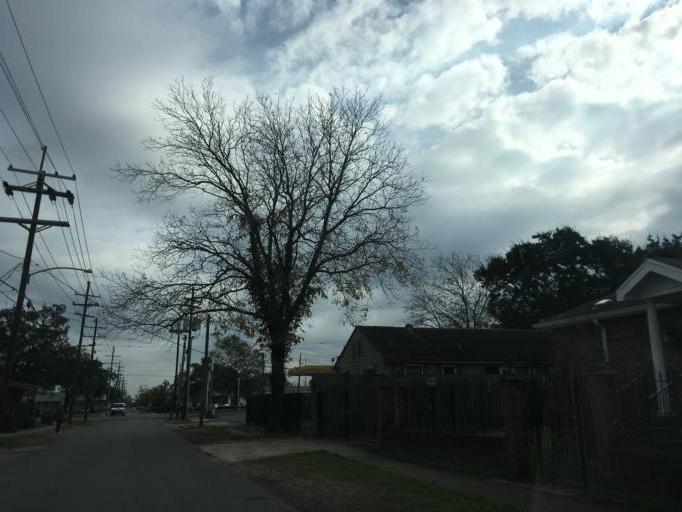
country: US
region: Louisiana
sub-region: Orleans Parish
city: New Orleans
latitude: 29.9898
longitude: -90.0597
